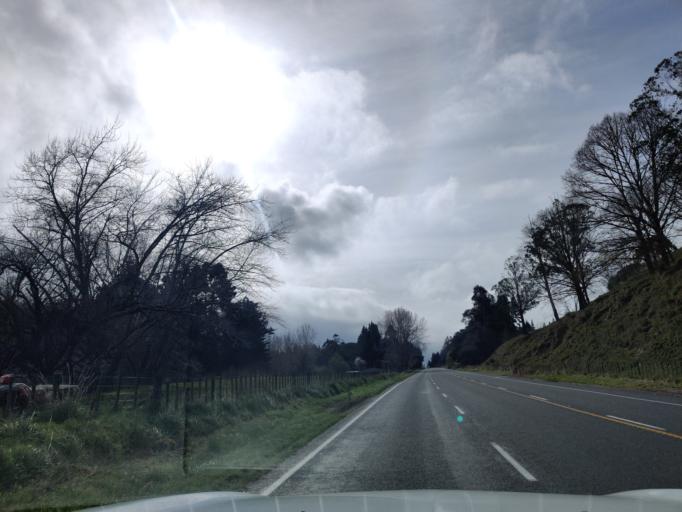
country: NZ
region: Manawatu-Wanganui
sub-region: Ruapehu District
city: Waiouru
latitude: -39.7744
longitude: 175.7912
